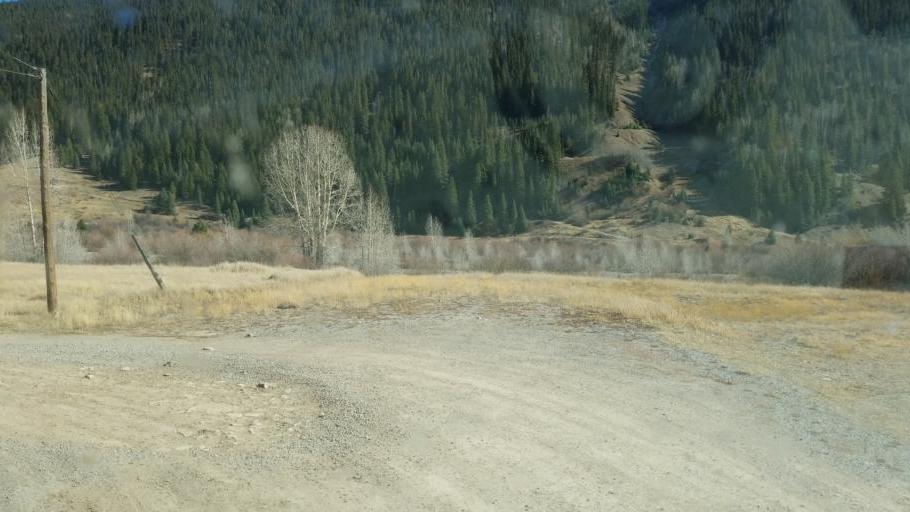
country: US
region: Colorado
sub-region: San Juan County
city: Silverton
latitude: 37.8107
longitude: -107.6607
